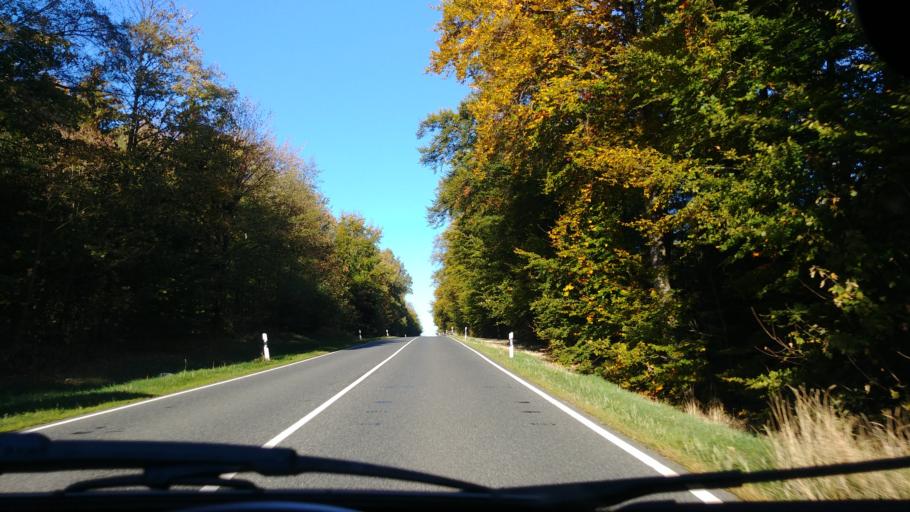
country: DE
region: Rheinland-Pfalz
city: Reckenroth
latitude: 50.1814
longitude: 7.9809
